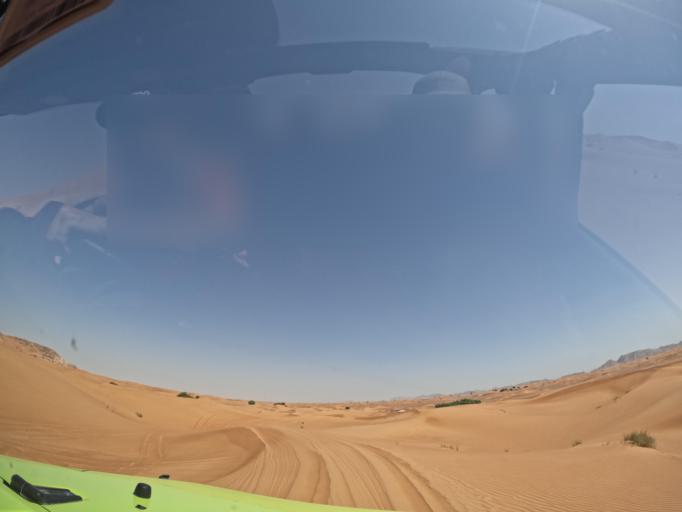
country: AE
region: Ash Shariqah
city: Adh Dhayd
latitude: 25.0091
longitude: 55.7363
